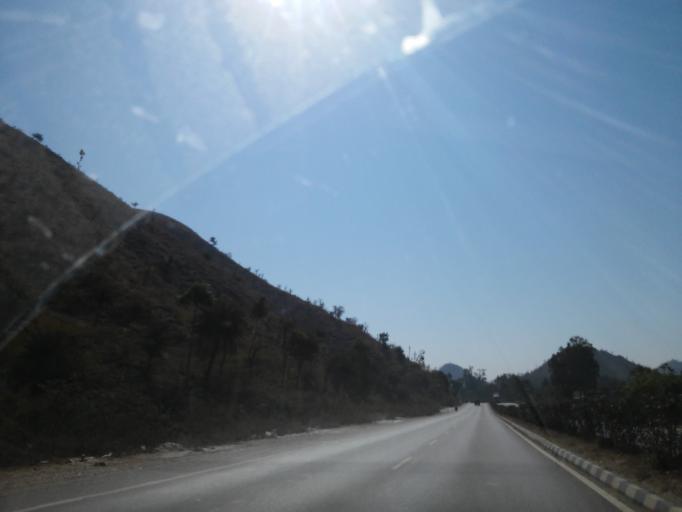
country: IN
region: Rajasthan
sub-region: Udaipur
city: Udaipur
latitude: 24.2154
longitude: 73.6961
